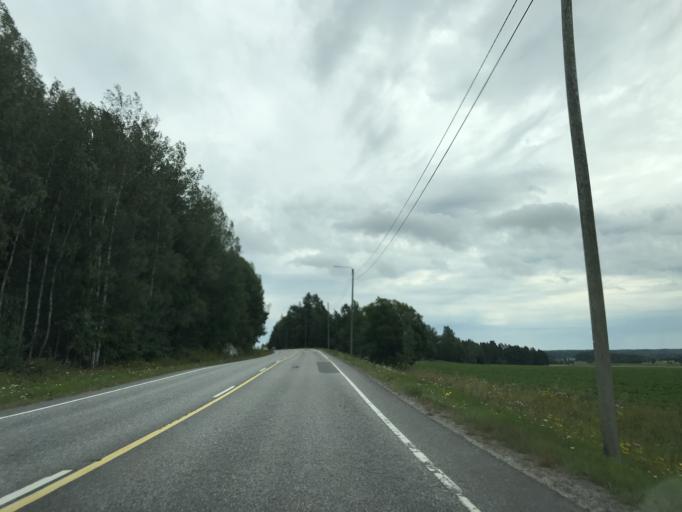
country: FI
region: Varsinais-Suomi
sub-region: Turku
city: Paimio
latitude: 60.4253
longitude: 22.6313
